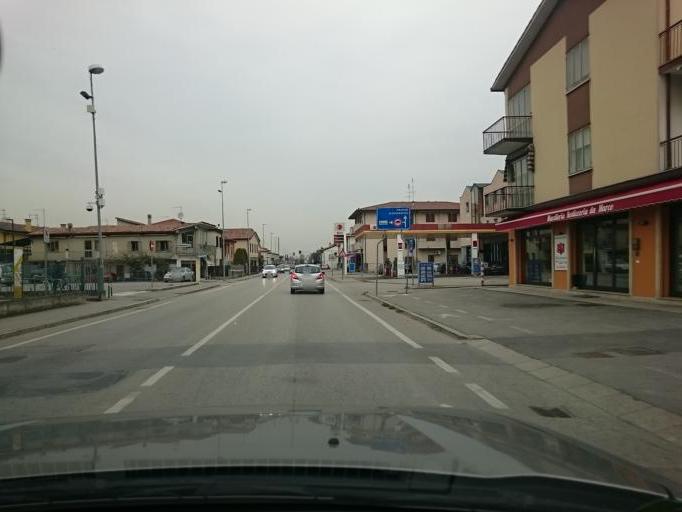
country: IT
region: Veneto
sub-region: Provincia di Padova
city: Masera di Padova
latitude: 45.3221
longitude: 11.8636
